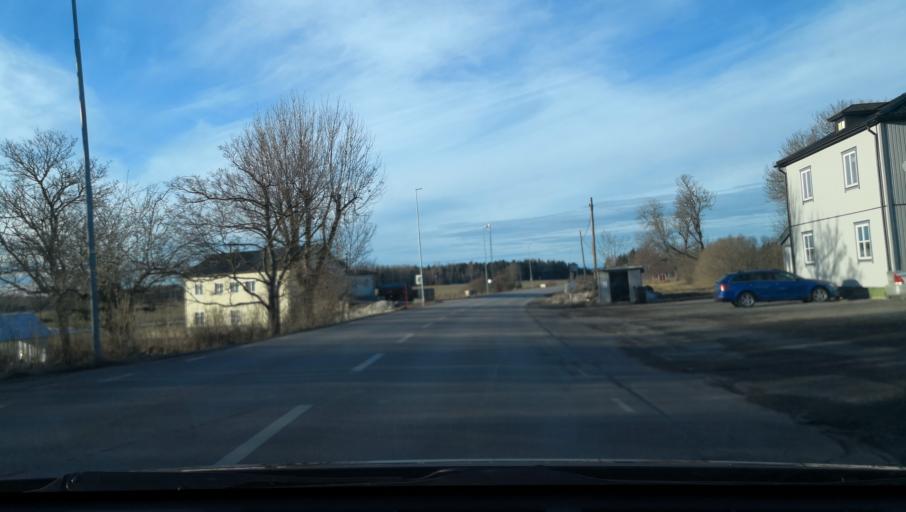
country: SE
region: Uppsala
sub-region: Osthammars Kommun
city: OEsthammar
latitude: 60.2880
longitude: 18.2862
